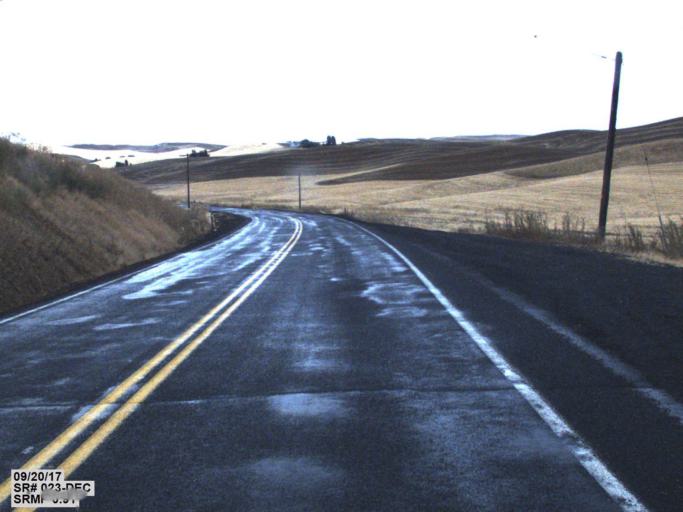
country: US
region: Washington
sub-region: Whitman County
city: Colfax
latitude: 47.0037
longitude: -117.3724
